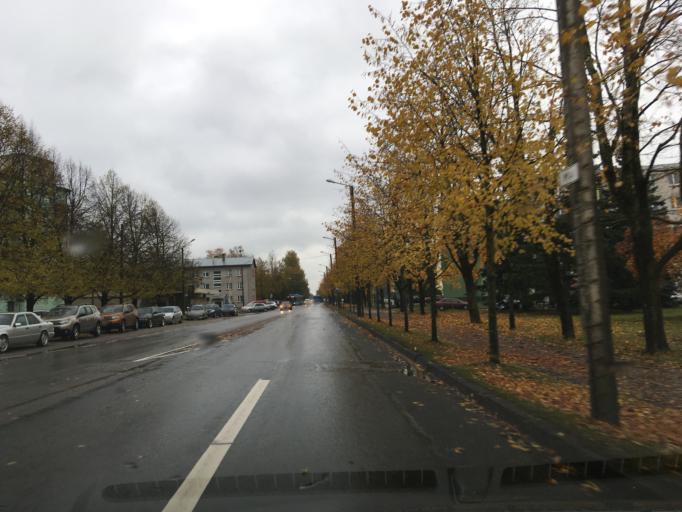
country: EE
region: Paernumaa
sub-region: Paernu linn
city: Parnu
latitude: 58.3738
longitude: 24.5315
